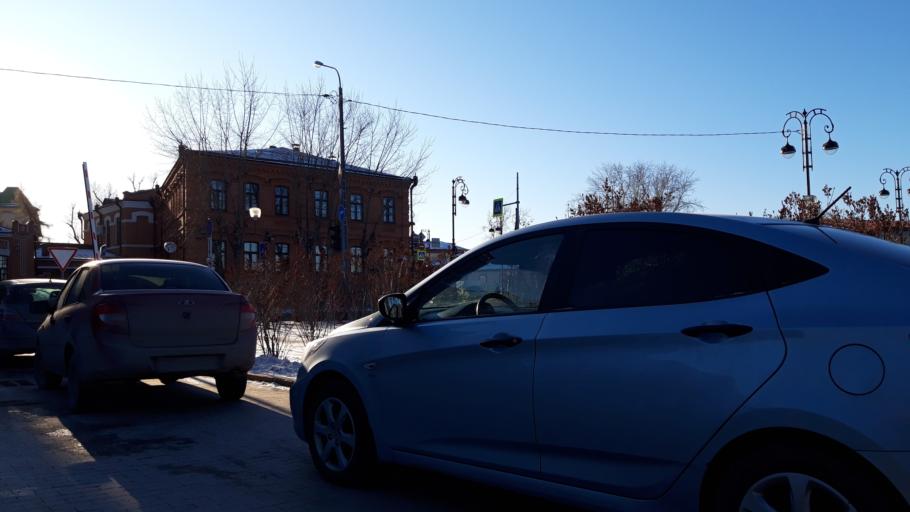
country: RU
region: Tjumen
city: Tyumen
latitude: 57.1602
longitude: 65.5429
